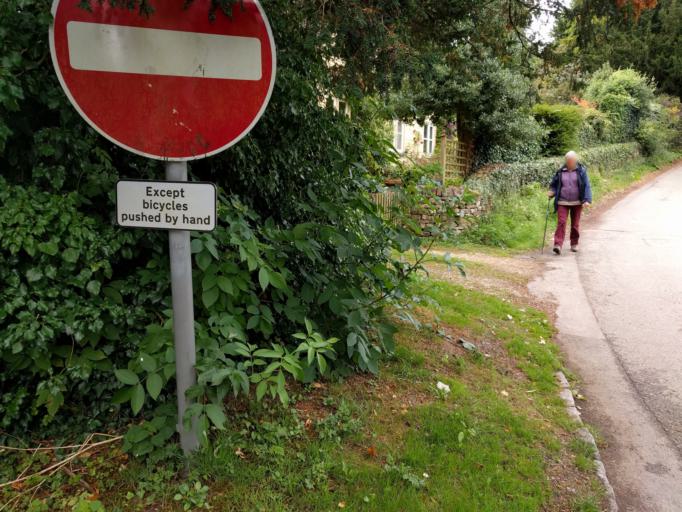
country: GB
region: England
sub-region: Gloucestershire
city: Chipping Campden
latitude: 52.0109
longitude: -1.7629
